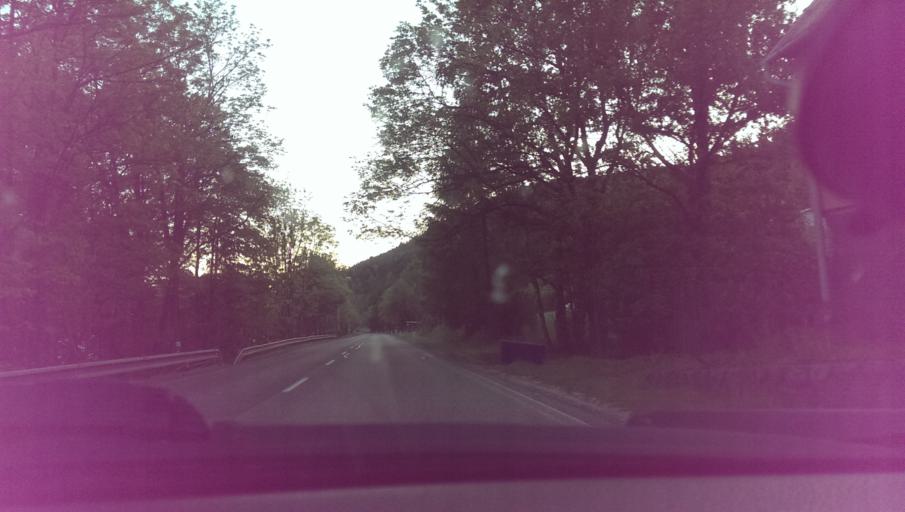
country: CZ
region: Zlin
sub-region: Okres Vsetin
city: Dolni Becva
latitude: 49.4950
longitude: 18.1774
